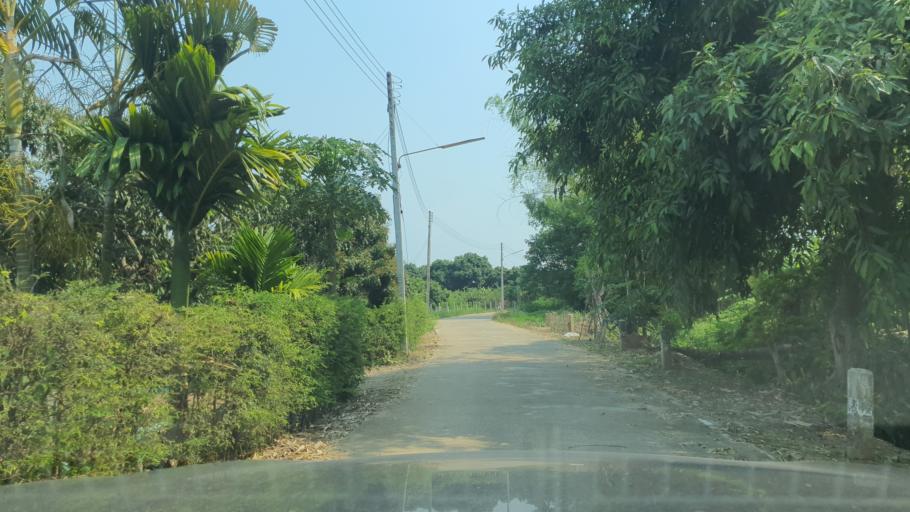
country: TH
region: Chiang Mai
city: Saraphi
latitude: 18.6598
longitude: 98.9905
